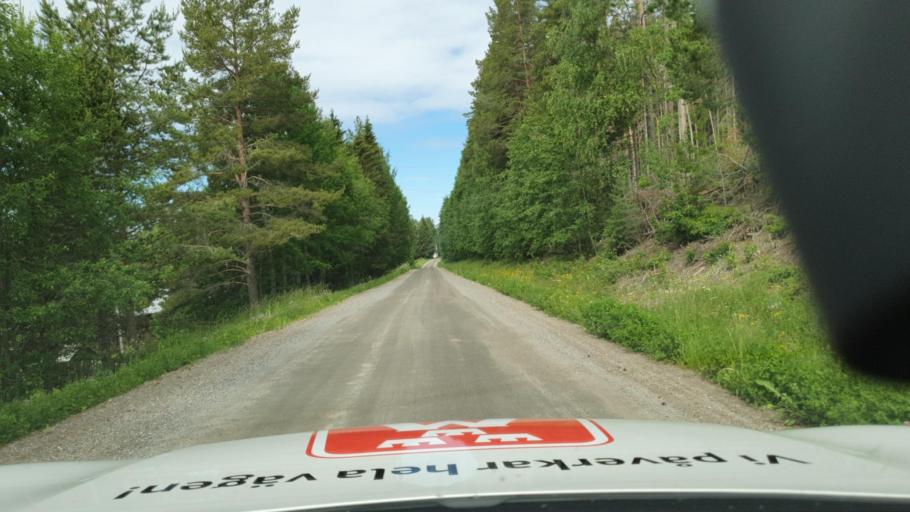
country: SE
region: Vaesterbotten
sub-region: Skelleftea Kommun
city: Burtraesk
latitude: 64.6223
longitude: 20.5632
